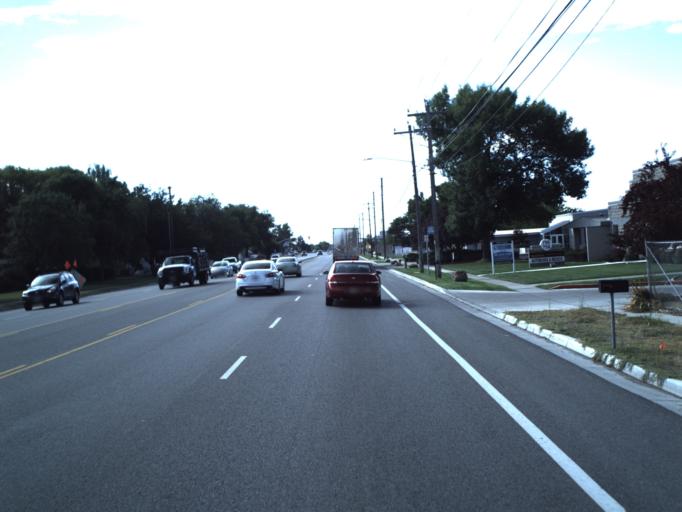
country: US
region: Utah
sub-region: Salt Lake County
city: Salt Lake City
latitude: 40.7541
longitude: -111.9391
